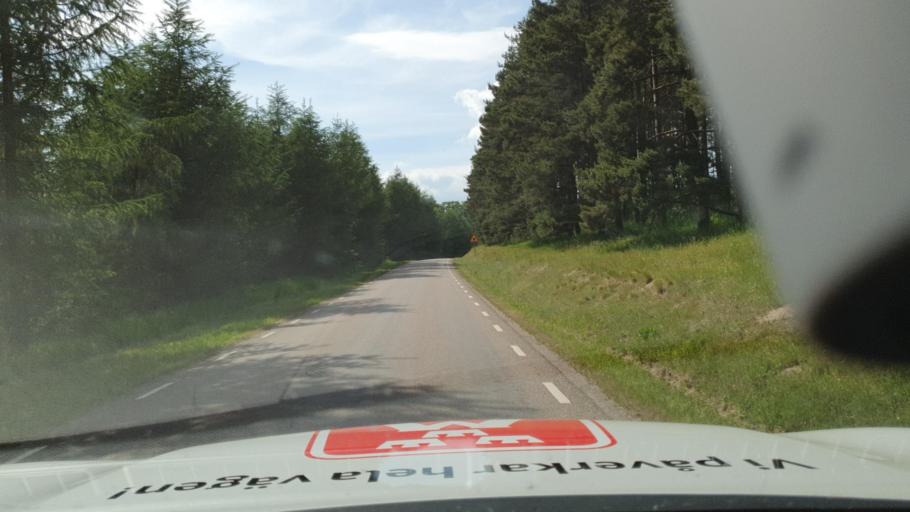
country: SE
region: Skane
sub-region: Skurups Kommun
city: Skurup
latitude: 55.5555
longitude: 13.5007
